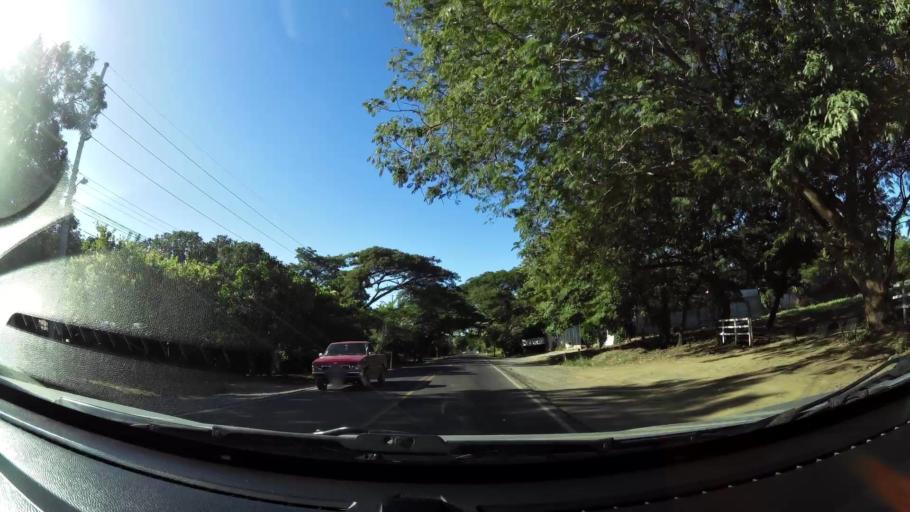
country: CR
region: Guanacaste
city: Belen
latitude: 10.4166
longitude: -85.5763
